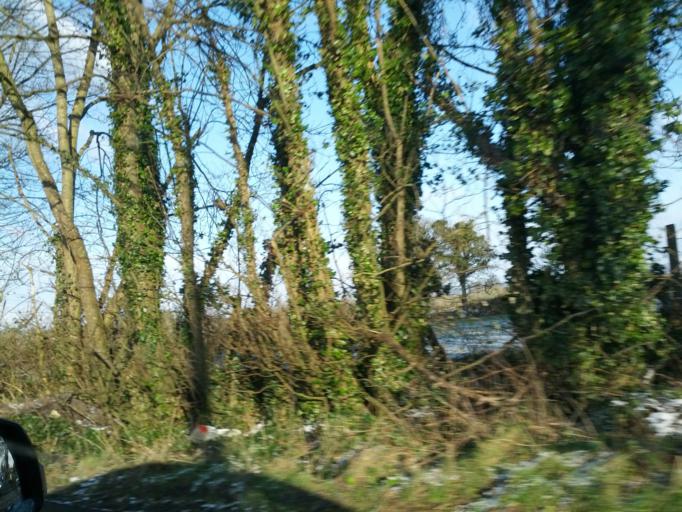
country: IE
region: Connaught
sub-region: County Galway
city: Gort
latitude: 53.1509
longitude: -8.7915
